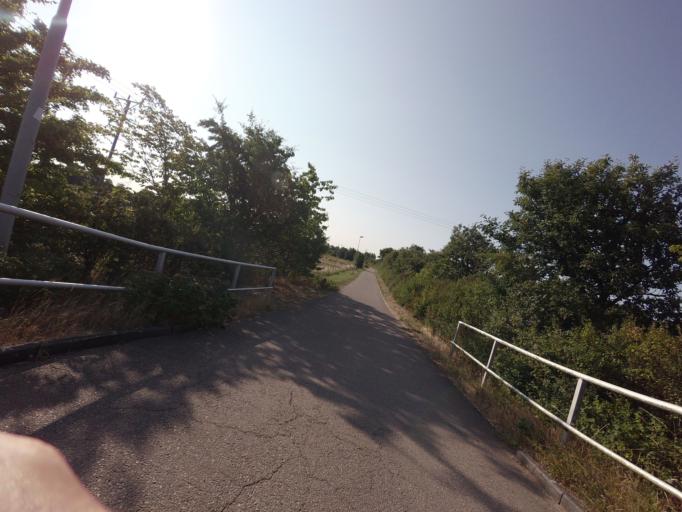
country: SE
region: Skane
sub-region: Landskrona
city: Asmundtorp
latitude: 55.8590
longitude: 12.8965
